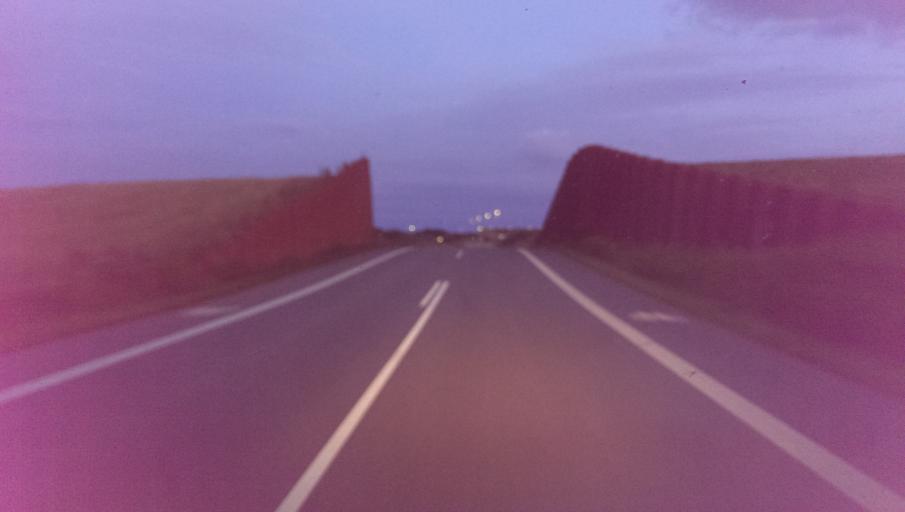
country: DK
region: South Denmark
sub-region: Esbjerg Kommune
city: Esbjerg
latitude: 55.5130
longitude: 8.4868
